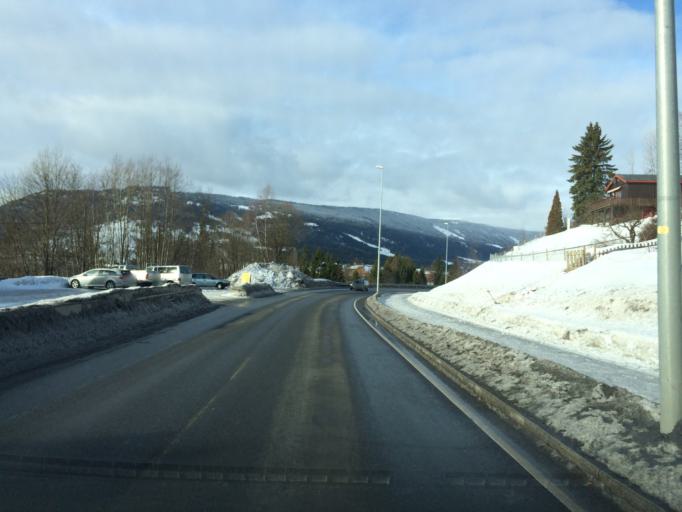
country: NO
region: Oppland
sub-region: Gausdal
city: Segalstad bru
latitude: 61.2252
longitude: 10.2301
